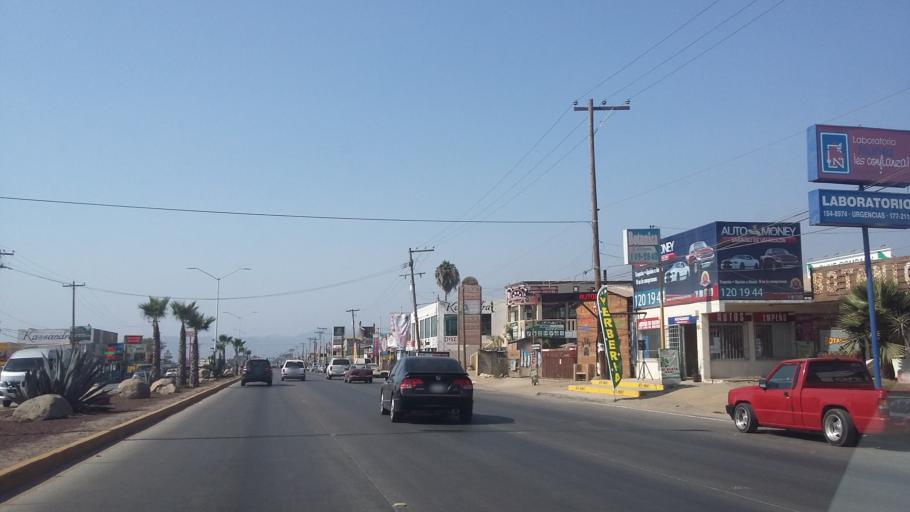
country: MX
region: Baja California
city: Rodolfo Sanchez Taboada
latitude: 31.7846
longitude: -116.5916
